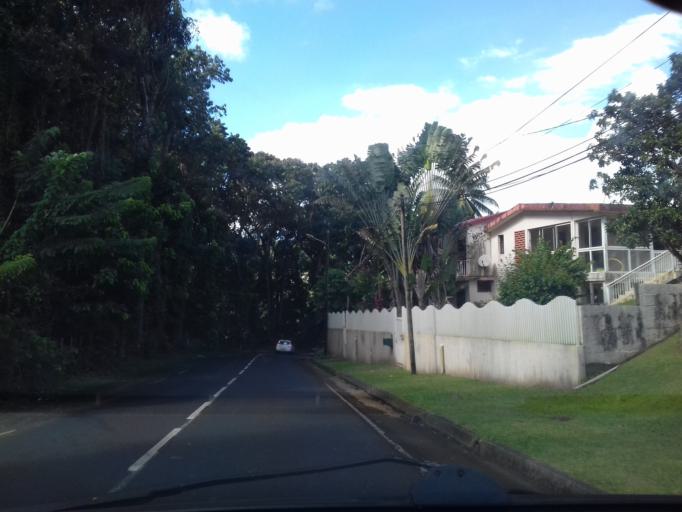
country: MQ
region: Martinique
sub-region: Martinique
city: Saint-Joseph
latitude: 14.6555
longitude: -61.0479
